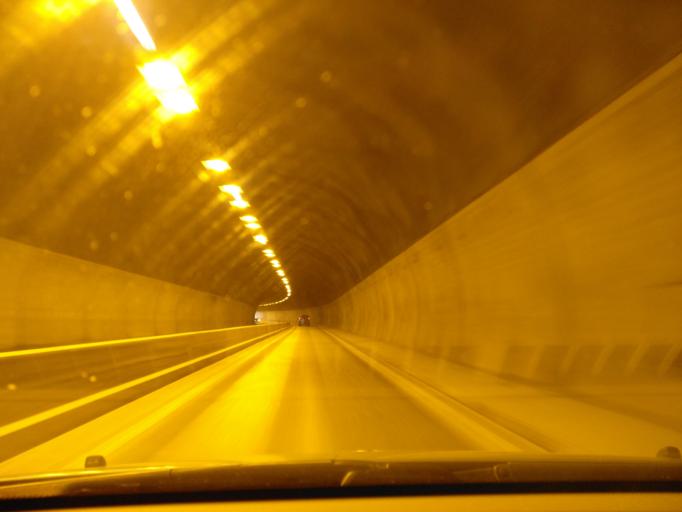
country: NO
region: Rogaland
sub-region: Tysvaer
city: Aksdal
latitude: 59.5073
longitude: 5.6149
